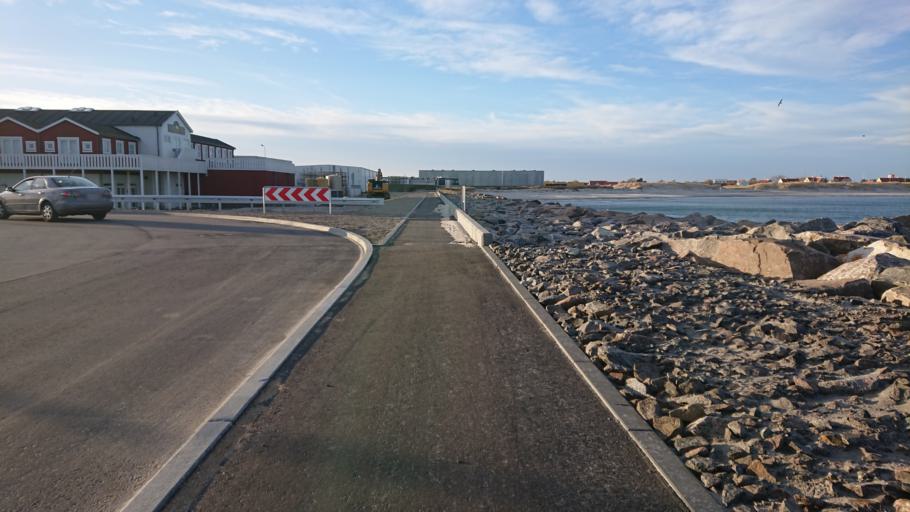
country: DK
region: North Denmark
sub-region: Frederikshavn Kommune
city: Skagen
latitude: 57.7206
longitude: 10.6069
